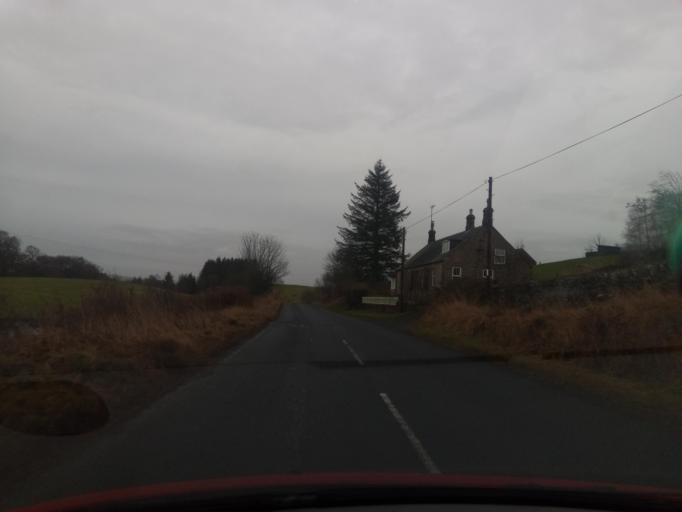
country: GB
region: England
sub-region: Northumberland
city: Rochester
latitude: 55.1654
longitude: -2.3702
